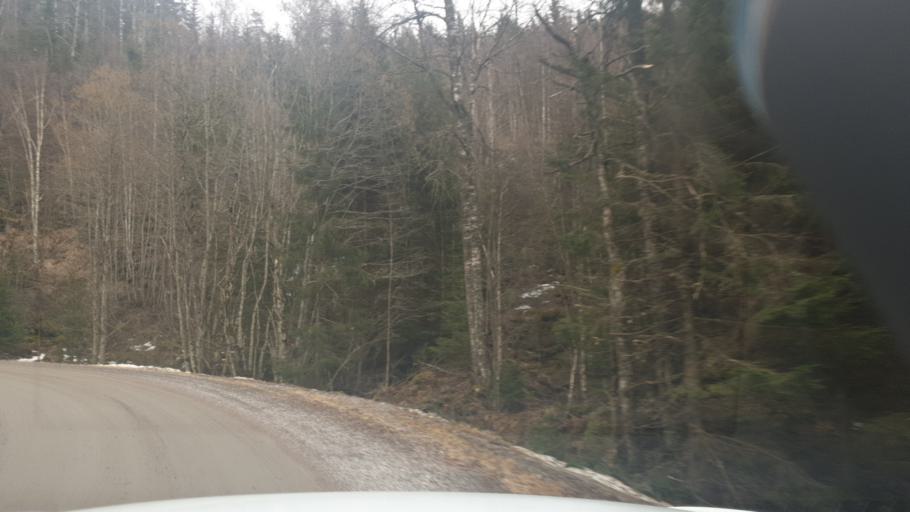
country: NO
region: Ostfold
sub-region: Romskog
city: Romskog
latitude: 59.7095
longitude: 11.9837
